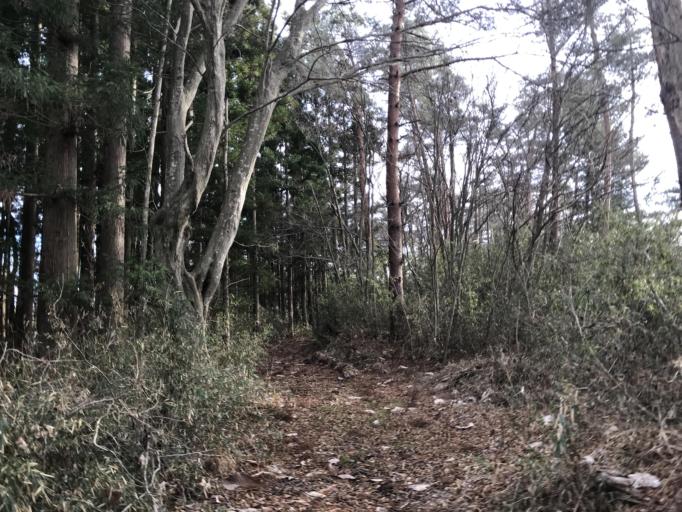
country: JP
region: Iwate
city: Ichinoseki
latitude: 38.8805
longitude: 141.1395
